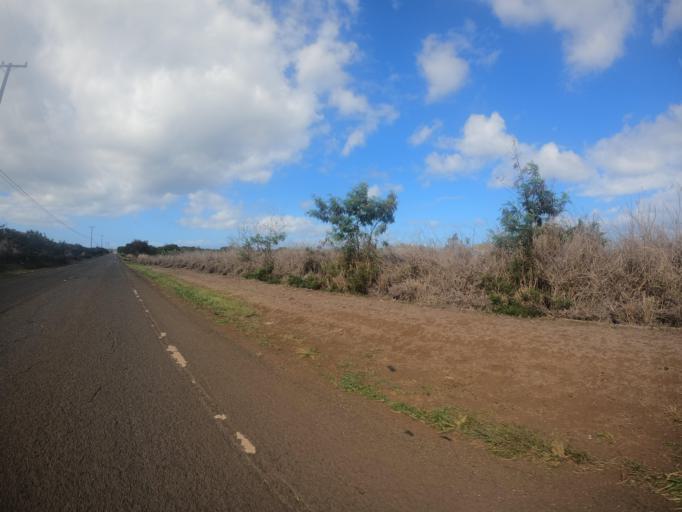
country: US
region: Hawaii
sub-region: Honolulu County
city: Waialua
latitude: 21.5712
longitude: -158.1425
